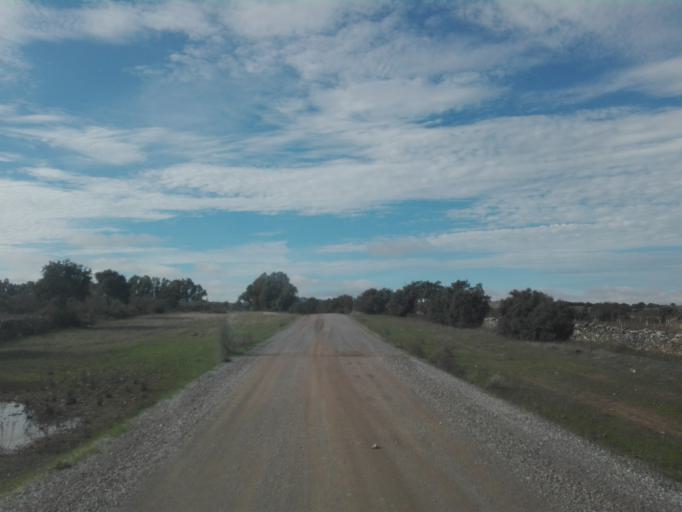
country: ES
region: Extremadura
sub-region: Provincia de Badajoz
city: Villagarcia de la Torre
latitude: 38.3003
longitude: -6.0941
